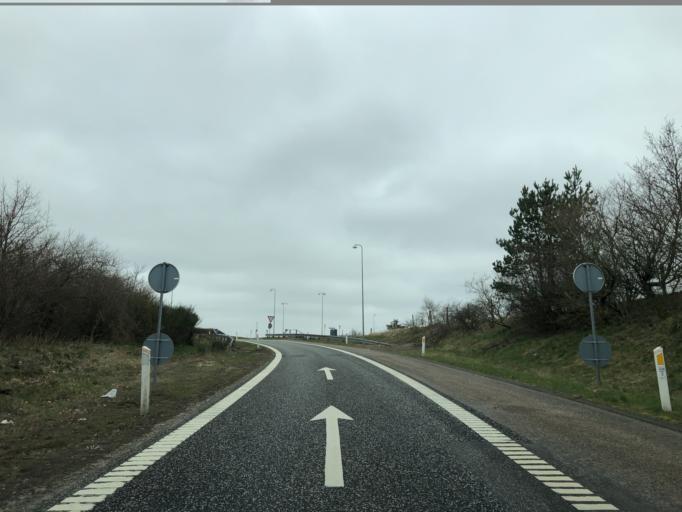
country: DK
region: North Denmark
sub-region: Frederikshavn Kommune
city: Saeby
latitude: 57.3129
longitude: 10.4484
